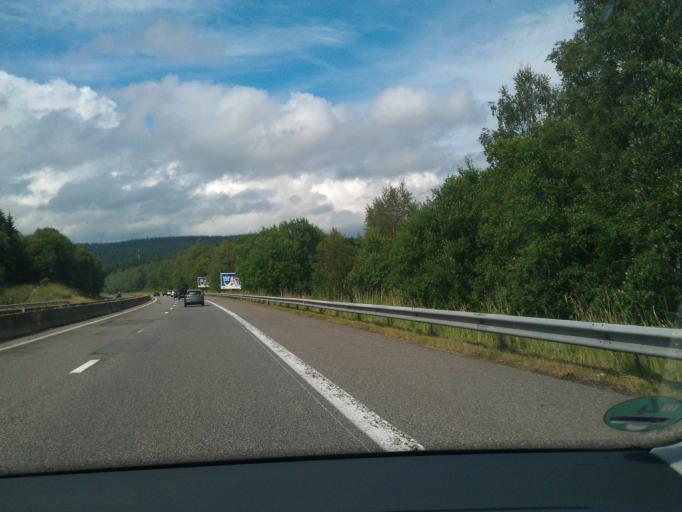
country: BE
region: Wallonia
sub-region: Province de Liege
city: Saint-Vith
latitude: 50.3307
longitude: 6.0909
